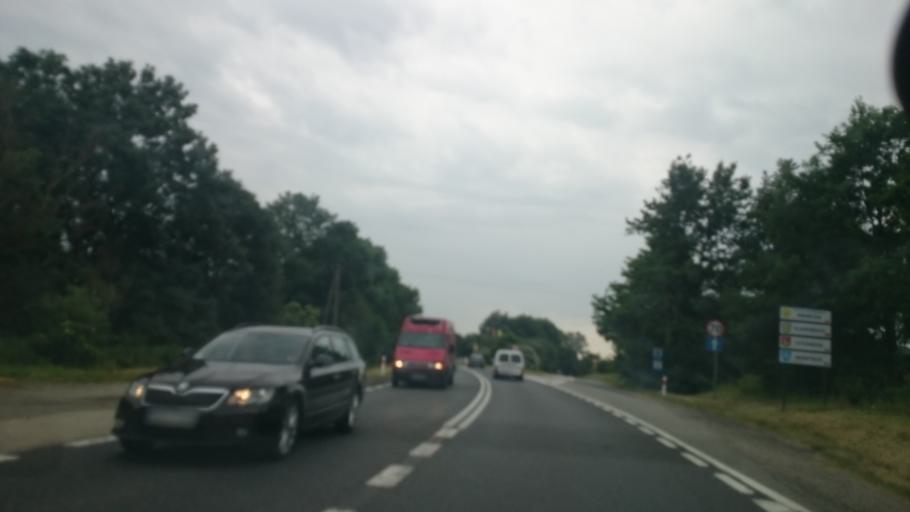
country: PL
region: Lower Silesian Voivodeship
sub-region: Powiat dzierzoniowski
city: Niemcza
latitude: 50.7365
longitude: 16.8378
